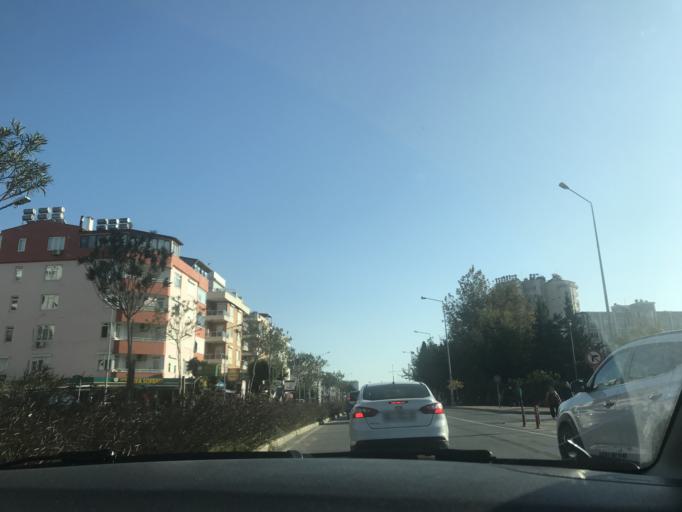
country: TR
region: Antalya
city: Antalya
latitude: 36.8813
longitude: 30.6495
